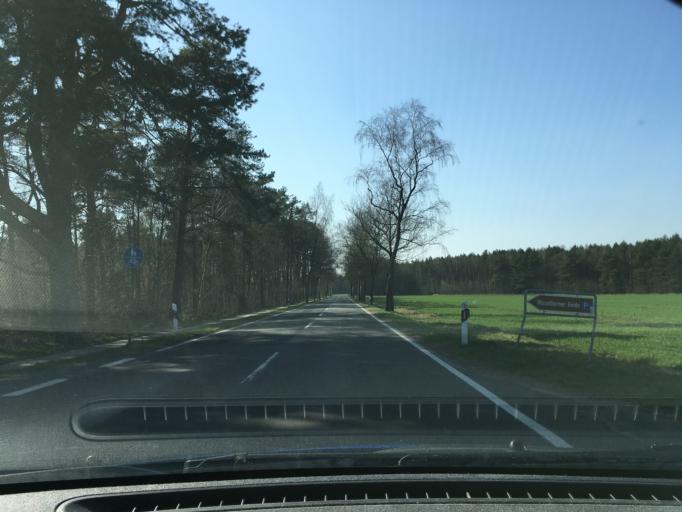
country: DE
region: Lower Saxony
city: Hermannsburg
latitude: 52.8234
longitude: 10.1369
